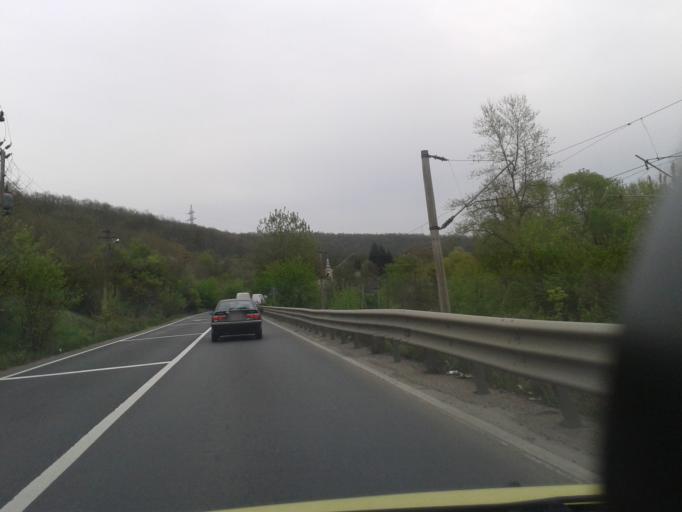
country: RO
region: Arad
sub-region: Comuna Bata
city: Bata
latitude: 46.0499
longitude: 22.0537
